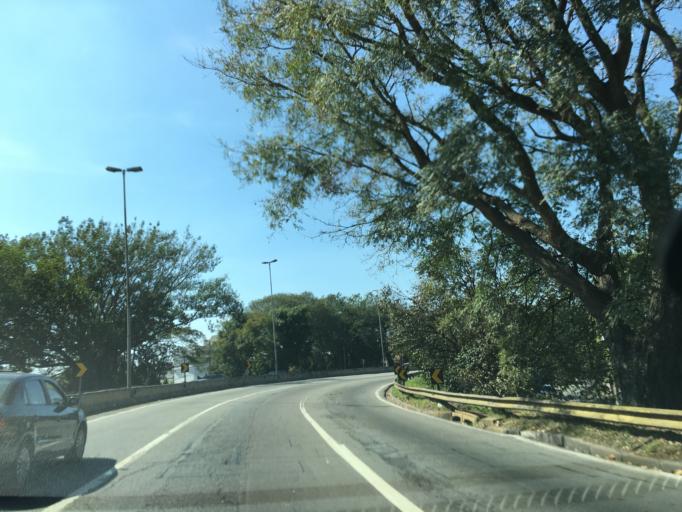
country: BR
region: Sao Paulo
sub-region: Osasco
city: Osasco
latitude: -23.5761
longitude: -46.7209
